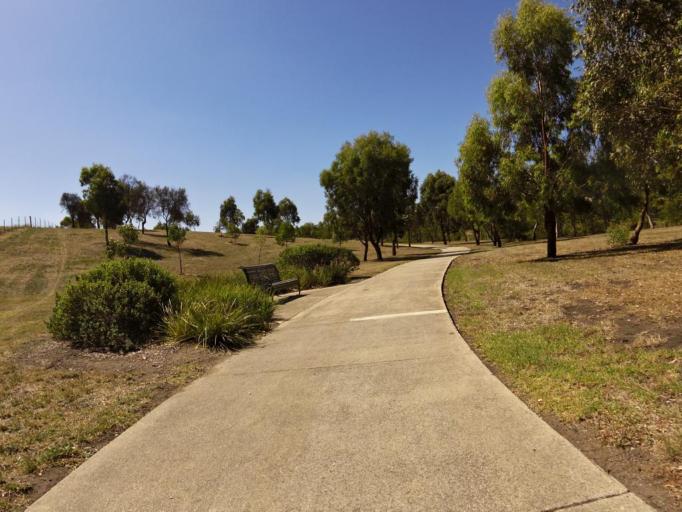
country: AU
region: Victoria
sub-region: Hume
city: Meadow Heights
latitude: -37.6472
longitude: 144.9056
